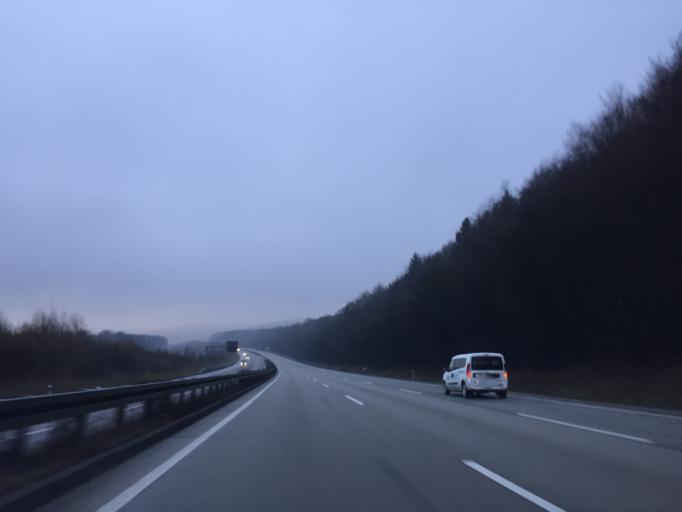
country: DE
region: Hesse
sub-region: Regierungsbezirk Darmstadt
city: Idstein
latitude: 50.2015
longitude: 8.2541
